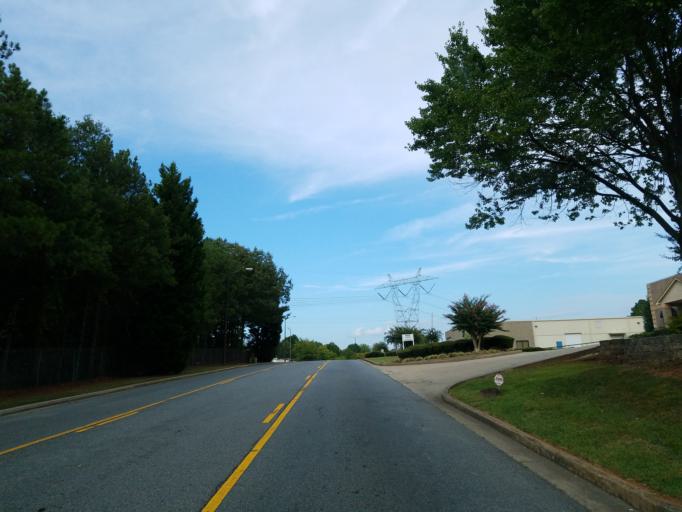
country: US
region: Georgia
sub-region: Cobb County
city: Marietta
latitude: 33.9959
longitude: -84.5361
